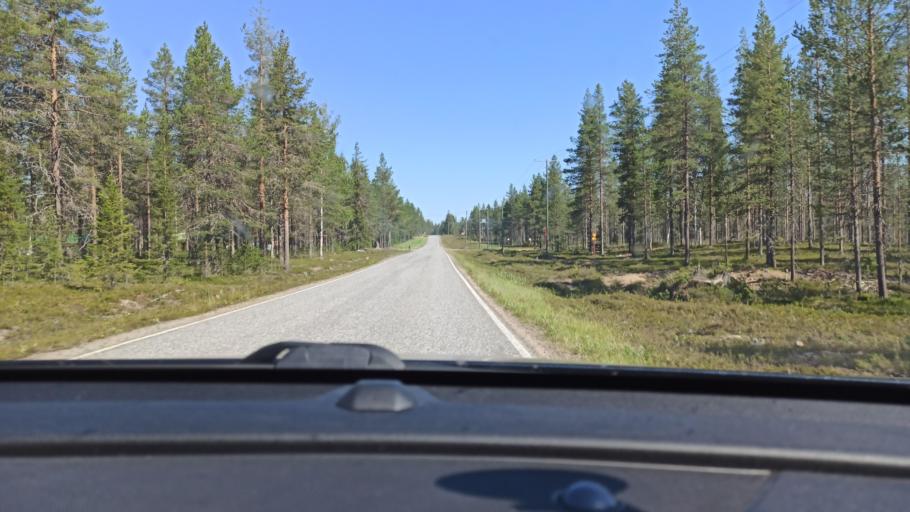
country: FI
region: Lapland
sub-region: Tunturi-Lappi
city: Kolari
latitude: 67.6511
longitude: 24.1622
